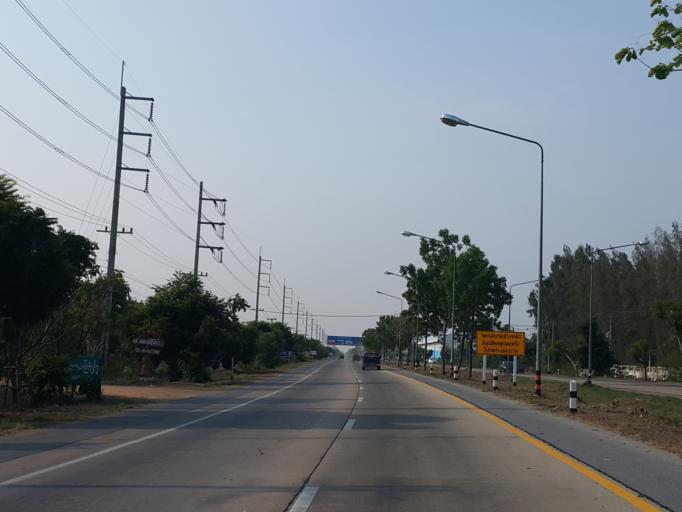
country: TH
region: Chai Nat
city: Hankha
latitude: 14.9470
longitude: 100.0818
